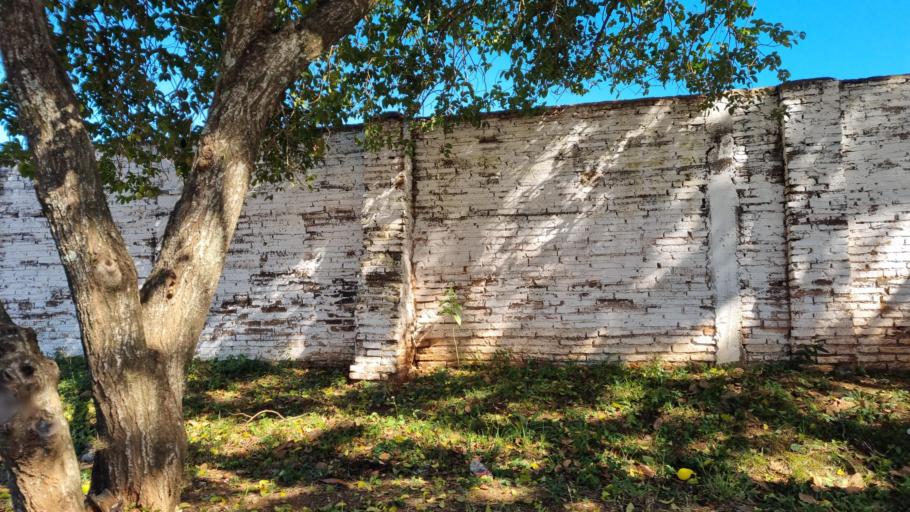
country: PY
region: Misiones
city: San Juan Bautista
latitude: -26.6755
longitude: -57.1447
